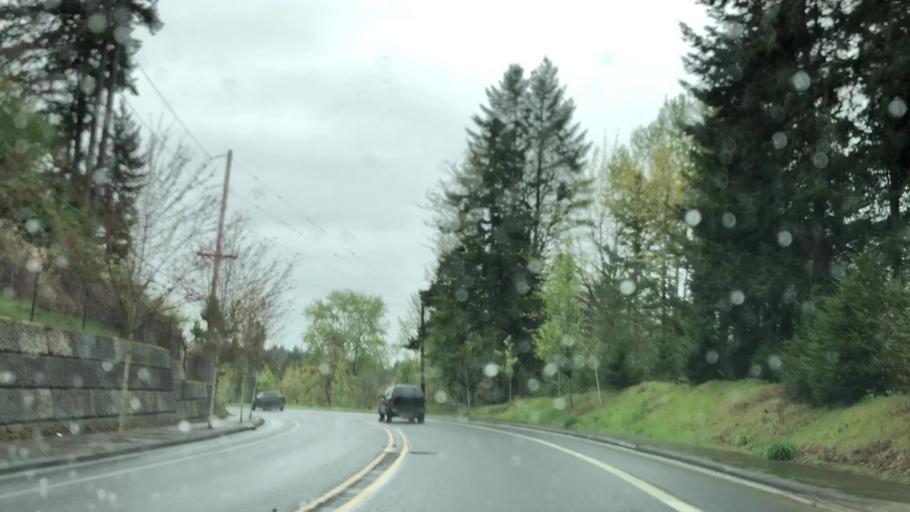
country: US
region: Oregon
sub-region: Washington County
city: Raleigh Hills
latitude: 45.4808
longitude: -122.7480
